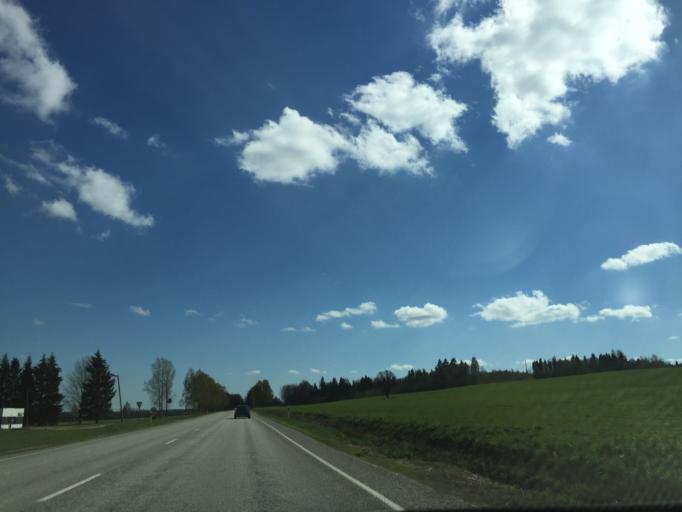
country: EE
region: Valgamaa
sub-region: Valga linn
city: Valga
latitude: 57.8947
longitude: 26.0534
